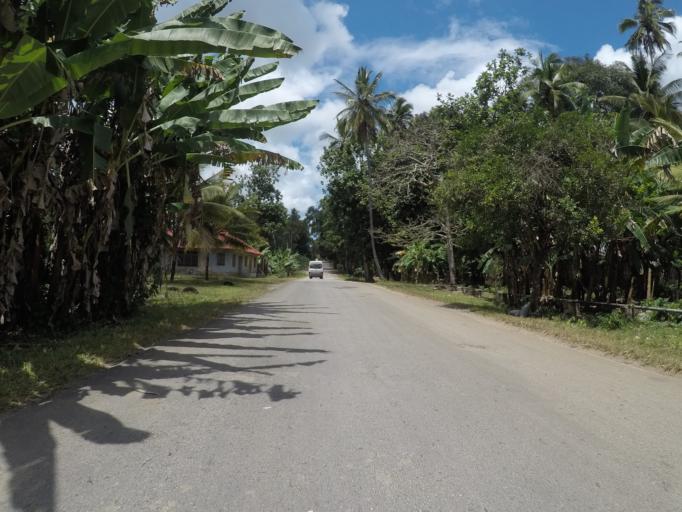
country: TZ
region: Zanzibar Central/South
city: Mahonda
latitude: -6.3043
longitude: 39.4320
